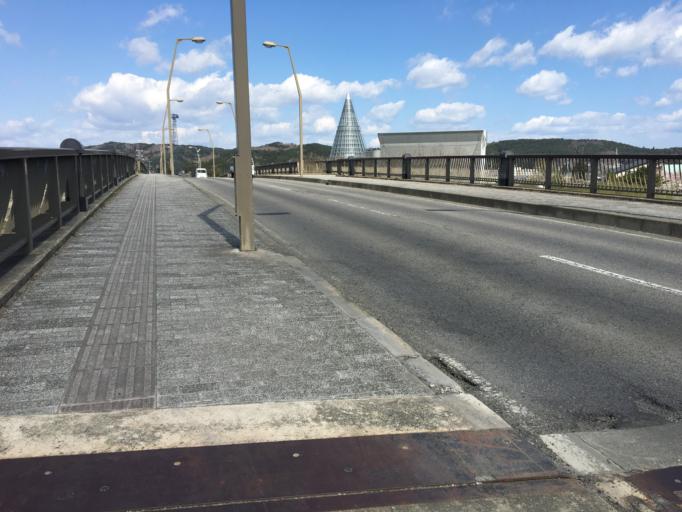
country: JP
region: Aomori
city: Hachinohe
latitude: 40.1897
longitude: 141.7792
